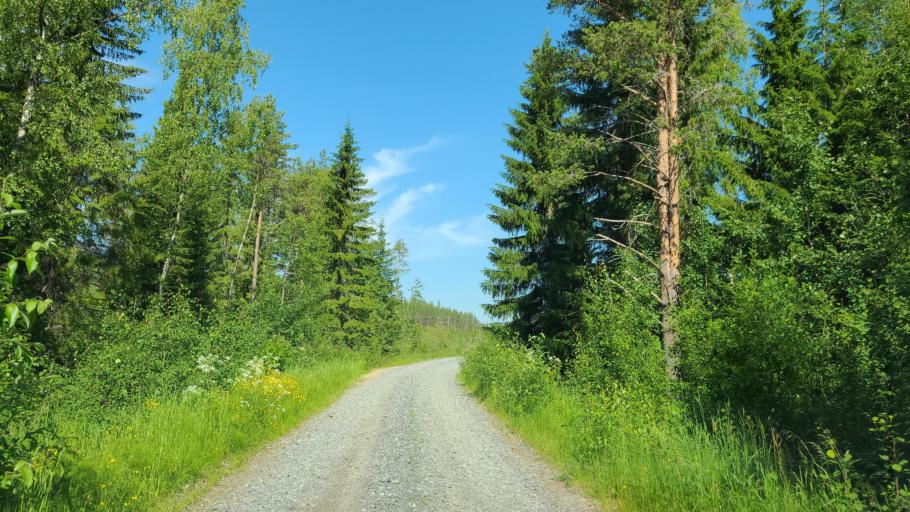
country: SE
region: Vaesterbotten
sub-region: Robertsfors Kommun
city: Robertsfors
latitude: 64.0909
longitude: 20.8363
